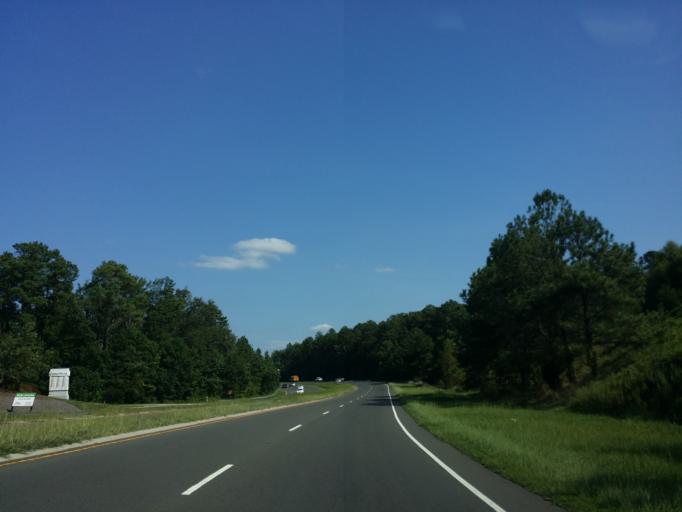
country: US
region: North Carolina
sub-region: Durham County
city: Durham
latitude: 35.9215
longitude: -78.8325
